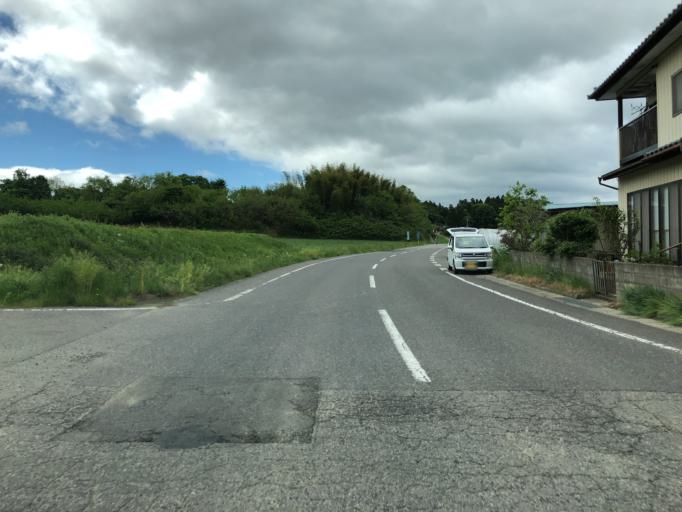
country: JP
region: Fukushima
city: Motomiya
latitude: 37.5111
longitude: 140.4748
